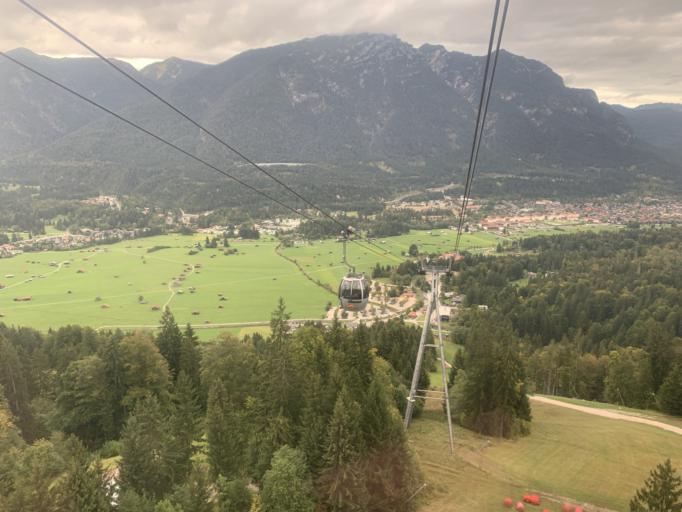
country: DE
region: Bavaria
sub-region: Upper Bavaria
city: Garmisch-Partenkirchen
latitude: 47.4644
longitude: 11.0650
